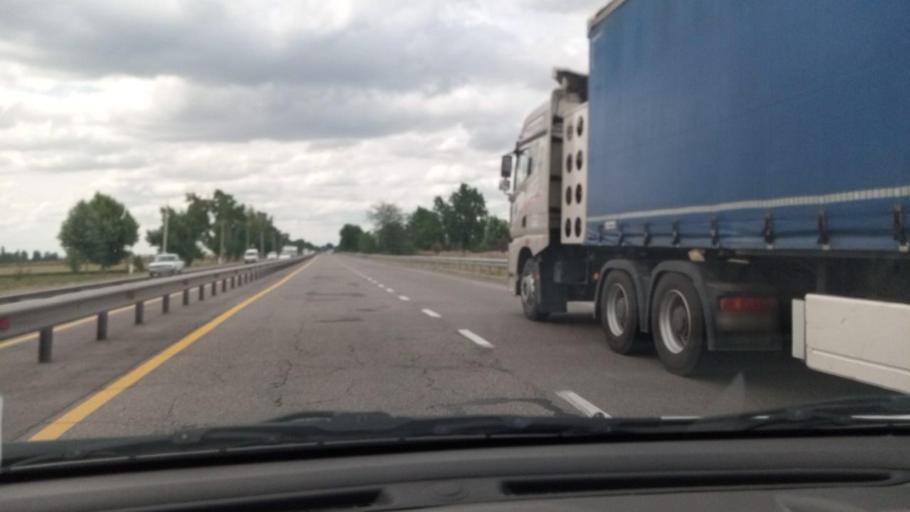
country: UZ
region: Toshkent Shahri
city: Bektemir
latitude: 41.1694
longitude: 69.4149
